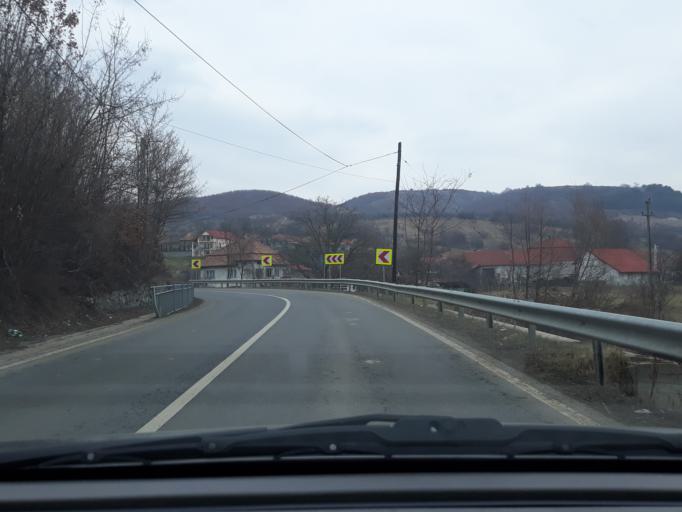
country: RO
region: Bihor
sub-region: Oras Alesd
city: Pestis
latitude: 47.0737
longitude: 22.4131
